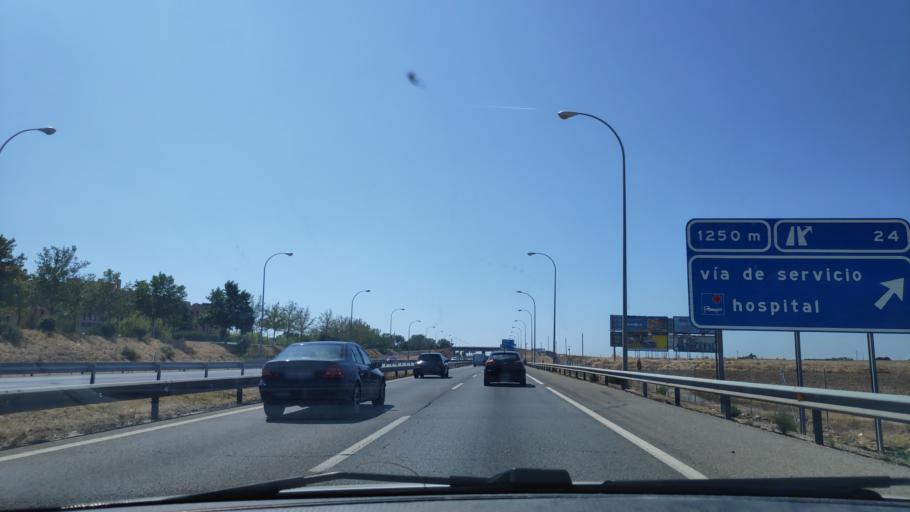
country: ES
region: Madrid
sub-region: Provincia de Madrid
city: Parla
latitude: 40.2401
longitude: -3.7807
